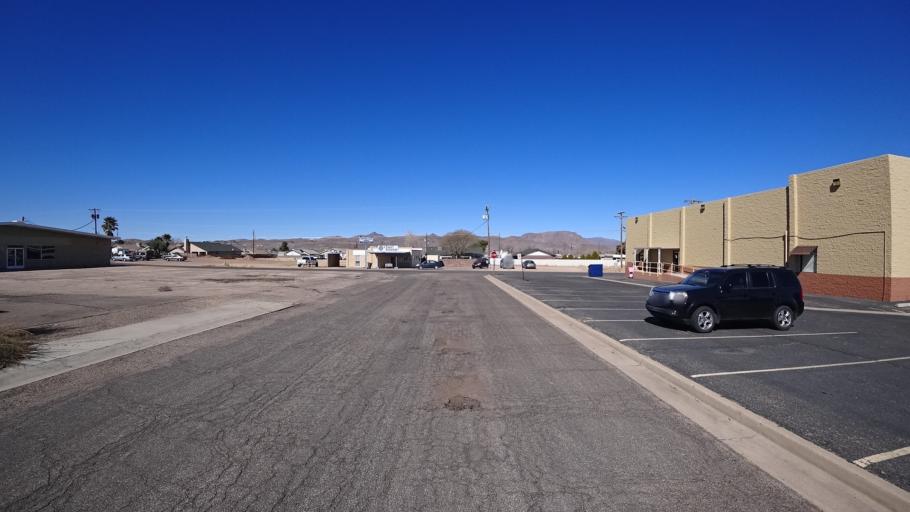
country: US
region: Arizona
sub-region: Mohave County
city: Kingman
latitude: 35.2096
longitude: -114.0187
